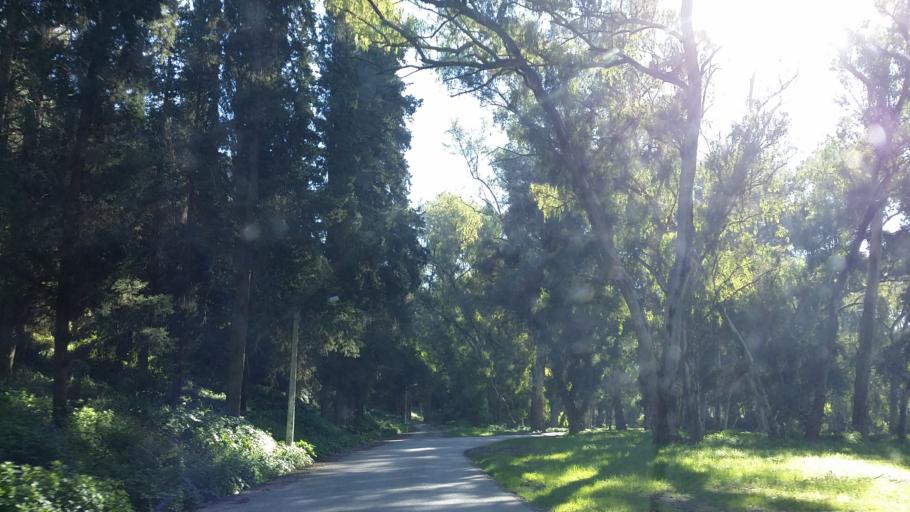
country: GR
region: West Greece
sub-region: Nomos Aitolias kai Akarnanias
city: Vonitsa
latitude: 38.9217
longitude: 20.8820
